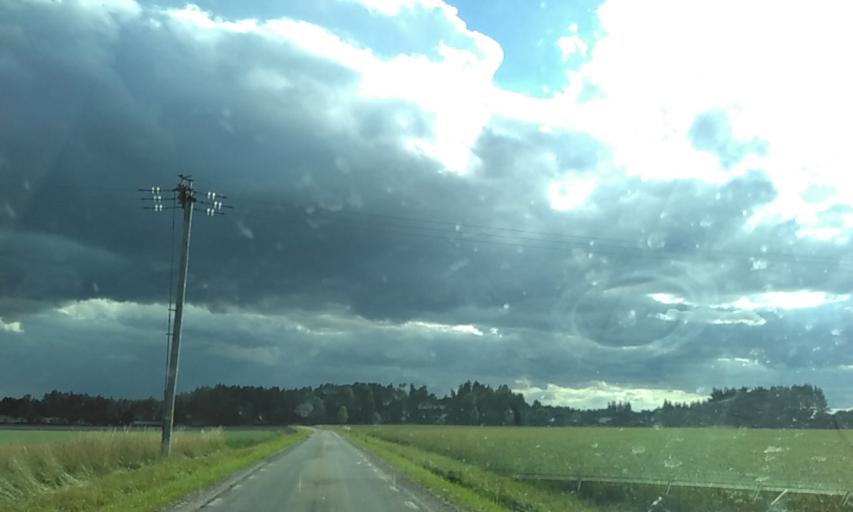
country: SE
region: Vaestra Goetaland
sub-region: Lidkopings Kommun
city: Lidkoping
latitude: 58.5605
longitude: 13.0158
